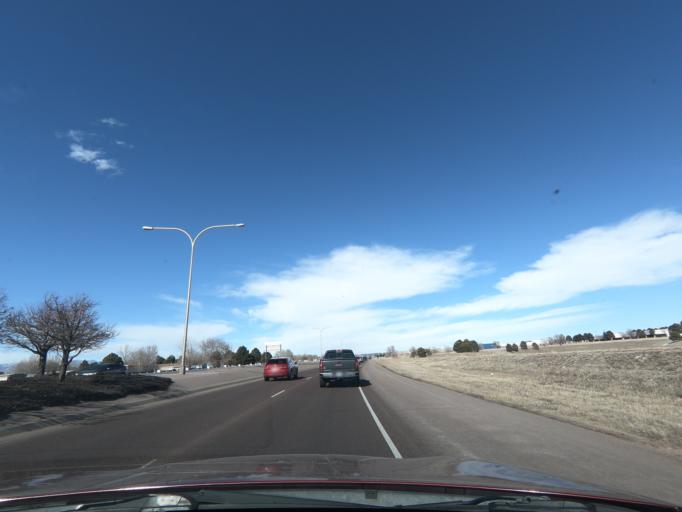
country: US
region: Colorado
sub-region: El Paso County
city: Security-Widefield
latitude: 38.7913
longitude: -104.7301
